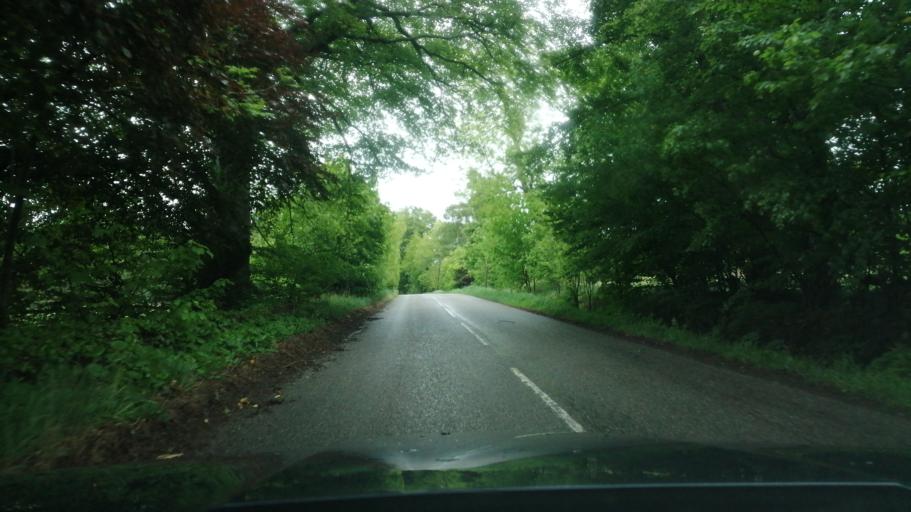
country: GB
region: Scotland
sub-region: Aberdeenshire
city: Huntly
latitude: 57.5427
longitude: -2.7962
